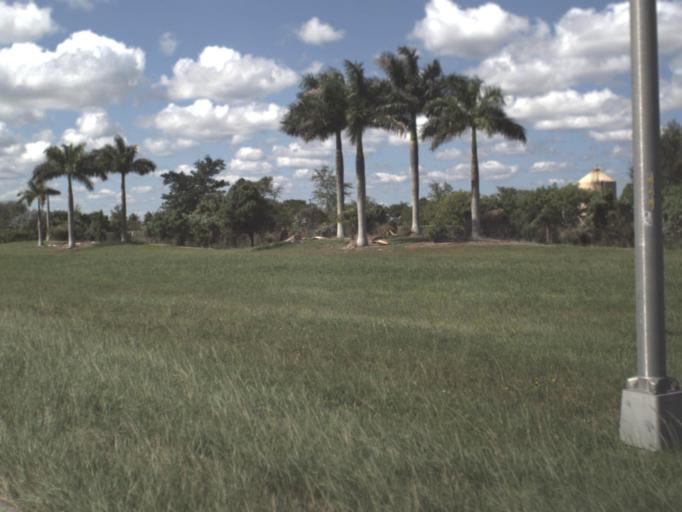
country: US
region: Florida
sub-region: Palm Beach County
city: Boca Pointe
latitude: 26.3044
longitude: -80.1548
